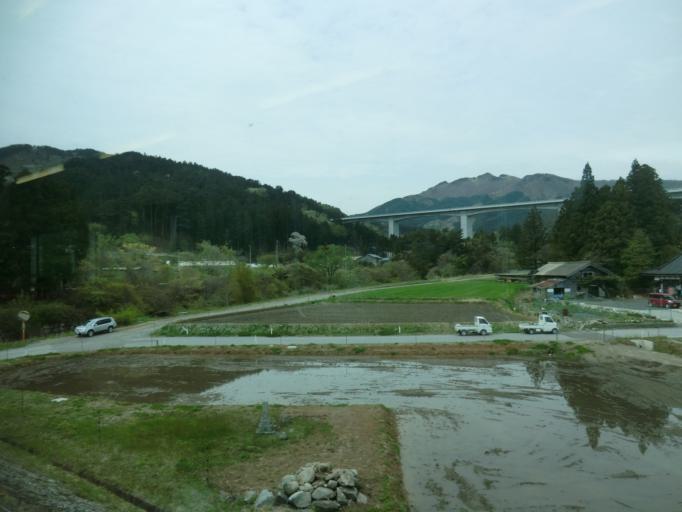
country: JP
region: Iwate
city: Ofunato
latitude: 39.1430
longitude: 141.8255
